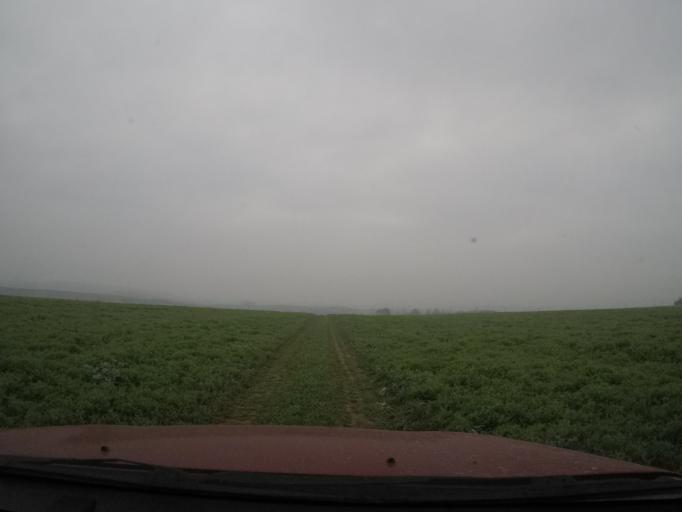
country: SK
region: Presovsky
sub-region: Okres Presov
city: Presov
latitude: 48.8865
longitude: 21.2707
